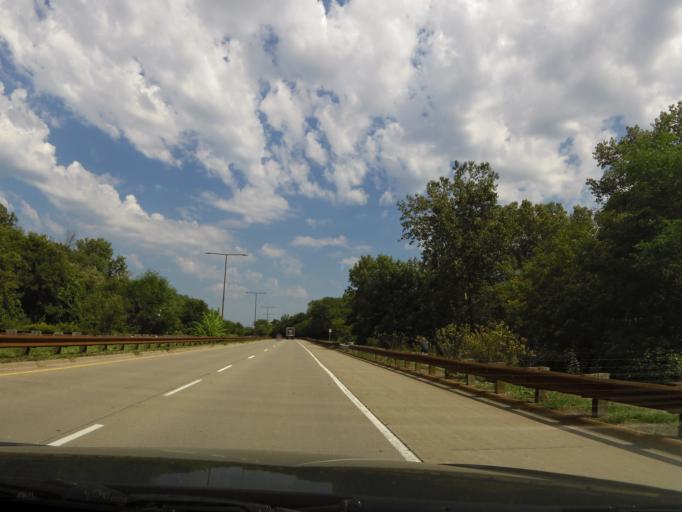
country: US
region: Minnesota
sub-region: Dakota County
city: Mendota Heights
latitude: 44.9130
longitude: -93.1389
